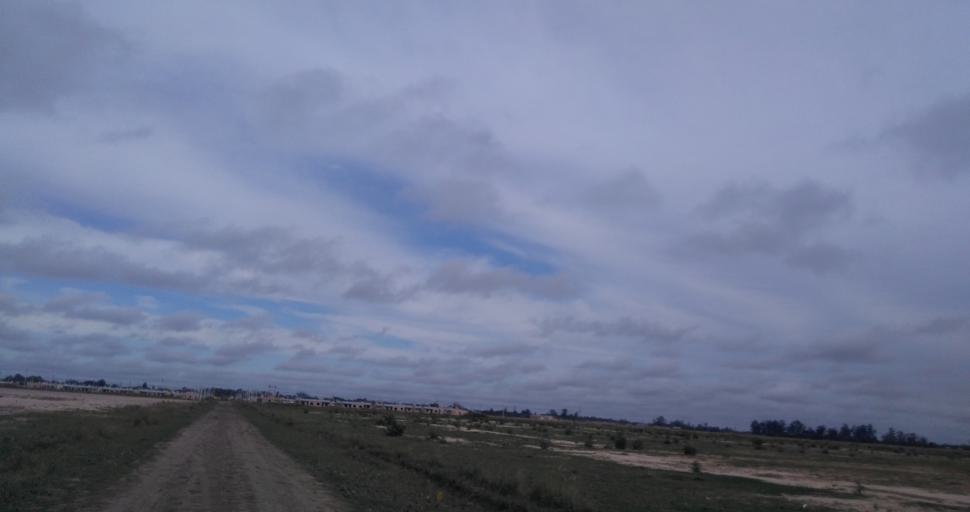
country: AR
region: Chaco
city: Fontana
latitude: -27.3916
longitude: -58.9845
